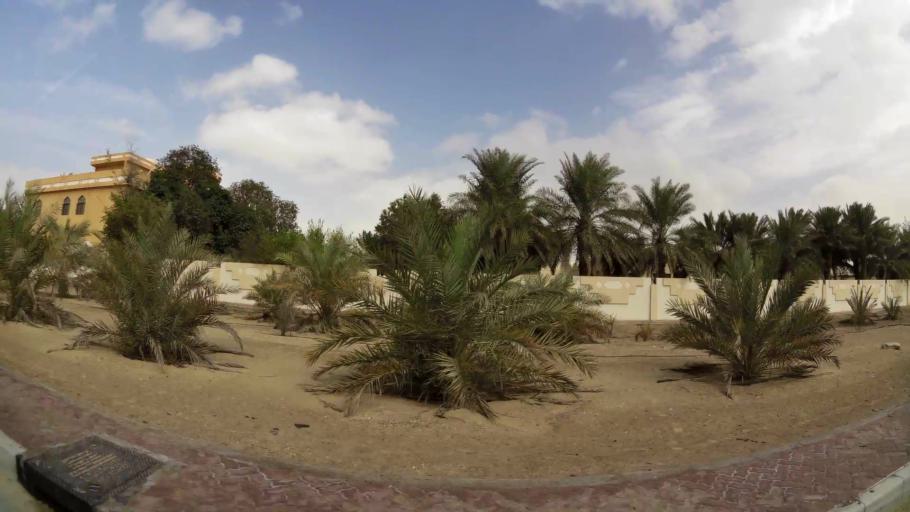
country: AE
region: Abu Dhabi
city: Abu Dhabi
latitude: 24.4012
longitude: 54.5059
